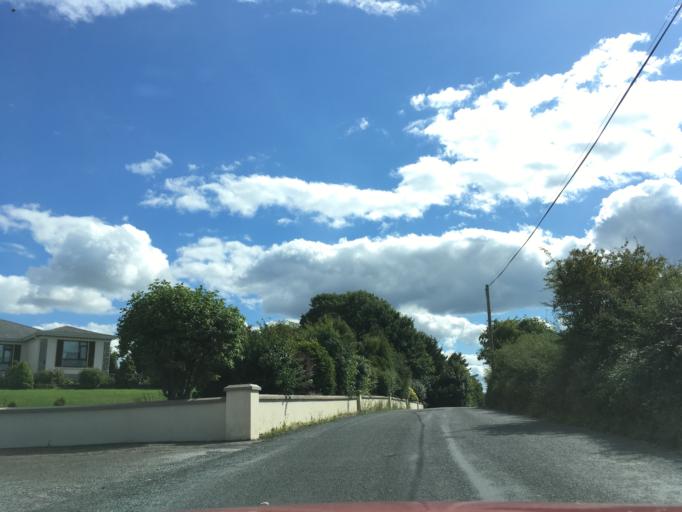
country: IE
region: Munster
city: Cashel
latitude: 52.4797
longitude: -7.9786
